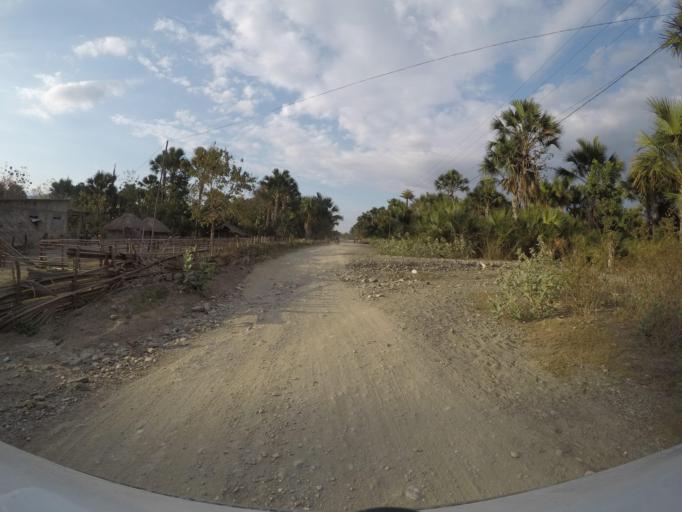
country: TL
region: Bobonaro
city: Maliana
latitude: -8.8612
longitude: 125.2169
